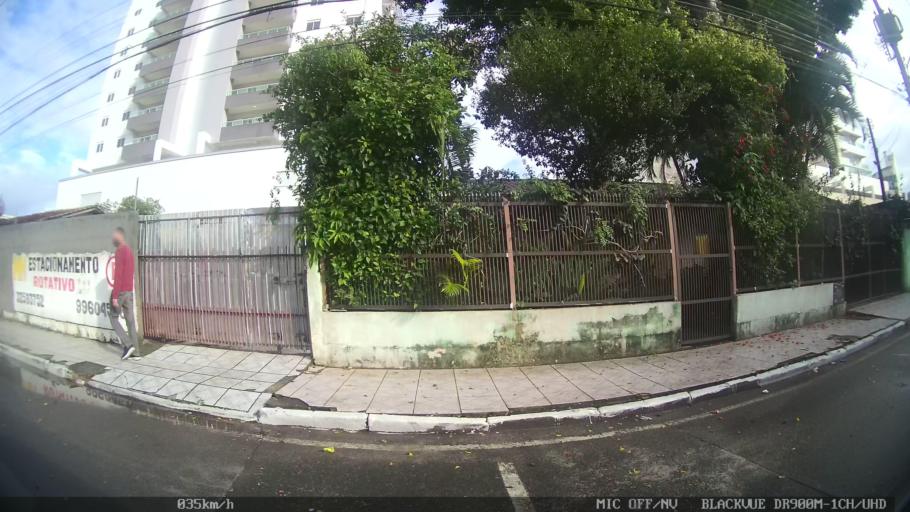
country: BR
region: Santa Catarina
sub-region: Sao Jose
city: Campinas
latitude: -27.5988
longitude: -48.6159
